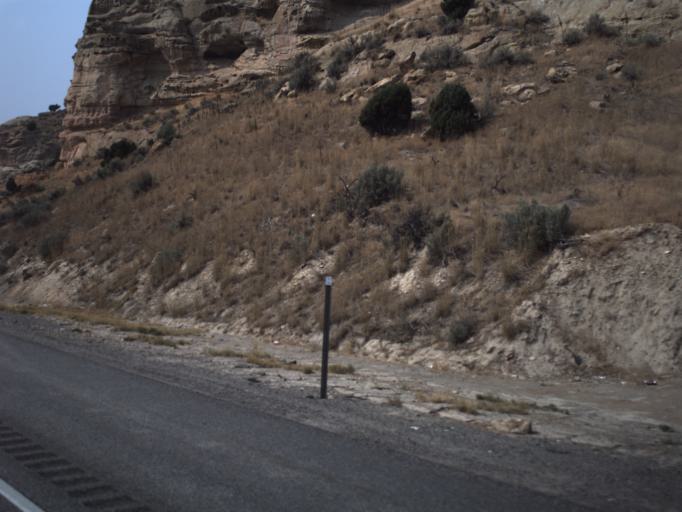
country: US
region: Wyoming
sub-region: Uinta County
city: Evanston
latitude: 41.1239
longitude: -111.1742
